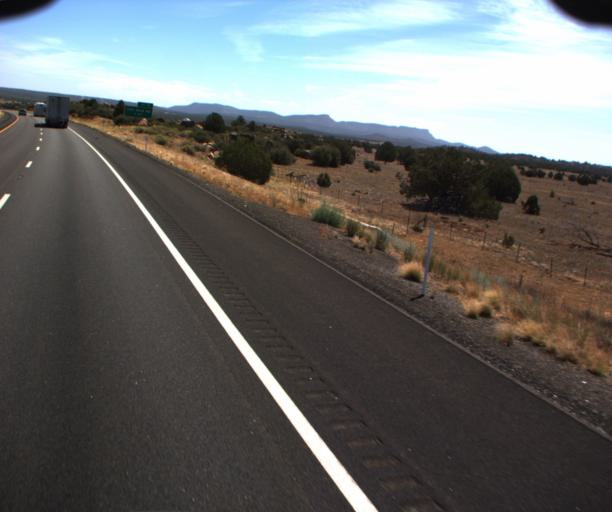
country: US
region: Arizona
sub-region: Mohave County
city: Peach Springs
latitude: 35.1841
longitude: -113.3855
